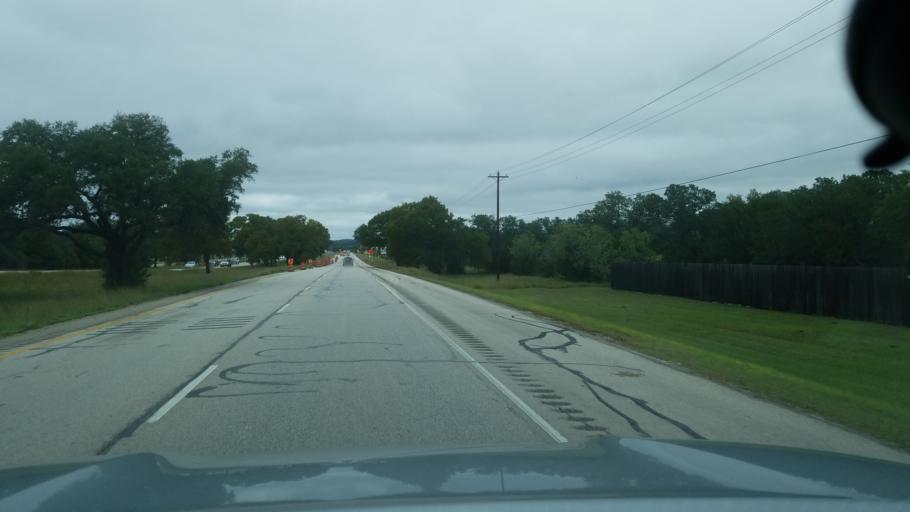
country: US
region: Texas
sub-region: Comal County
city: Bulverde
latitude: 29.8449
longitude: -98.4093
